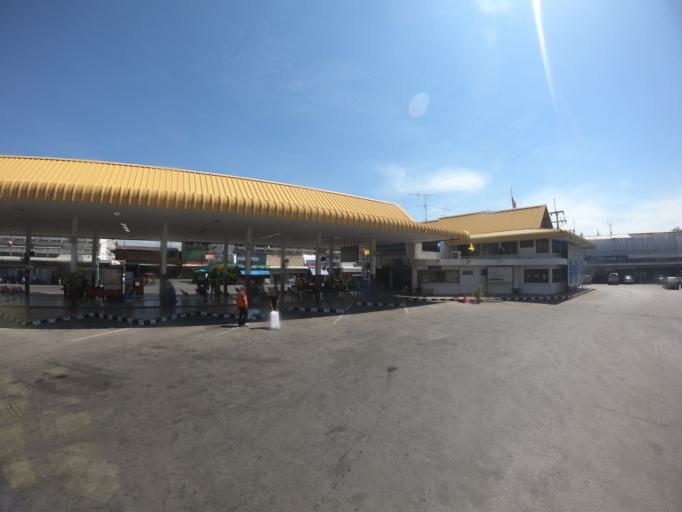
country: TH
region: Khon Kaen
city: Ban Phai
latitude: 16.0572
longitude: 102.7269
